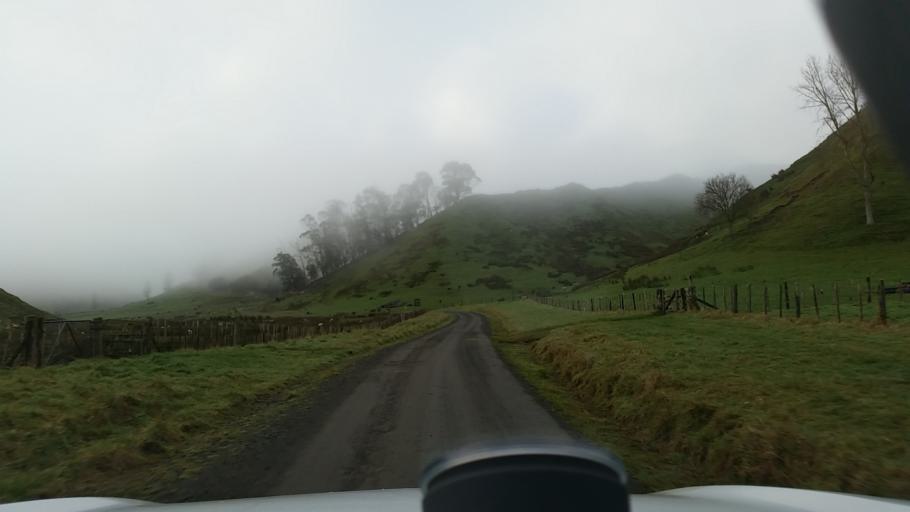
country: NZ
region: Taranaki
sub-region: South Taranaki District
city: Eltham
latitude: -39.4307
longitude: 174.4411
